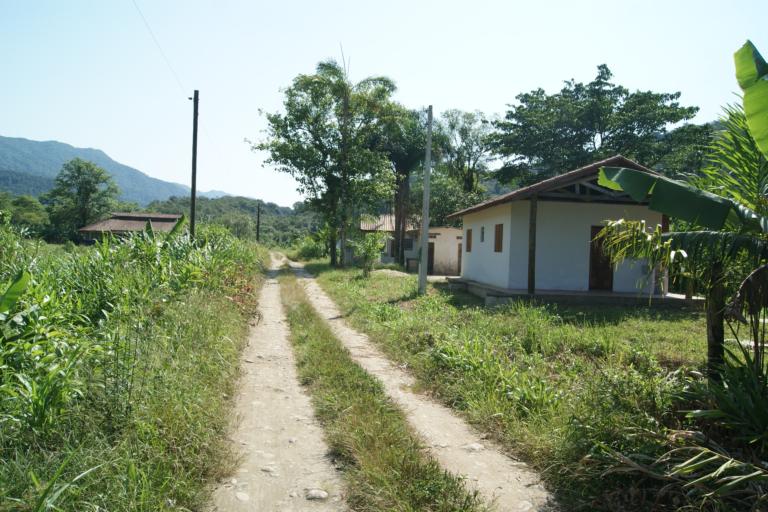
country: BR
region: Sao Paulo
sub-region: Mongagua
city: Mongagua
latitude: -24.0198
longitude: -46.6943
